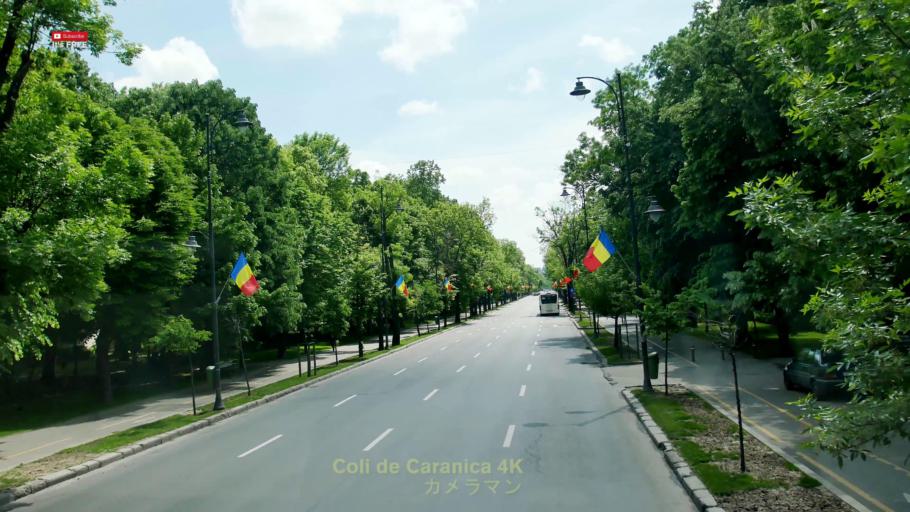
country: RO
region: Bucuresti
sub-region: Municipiul Bucuresti
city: Bucuresti
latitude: 44.4661
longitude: 26.0786
